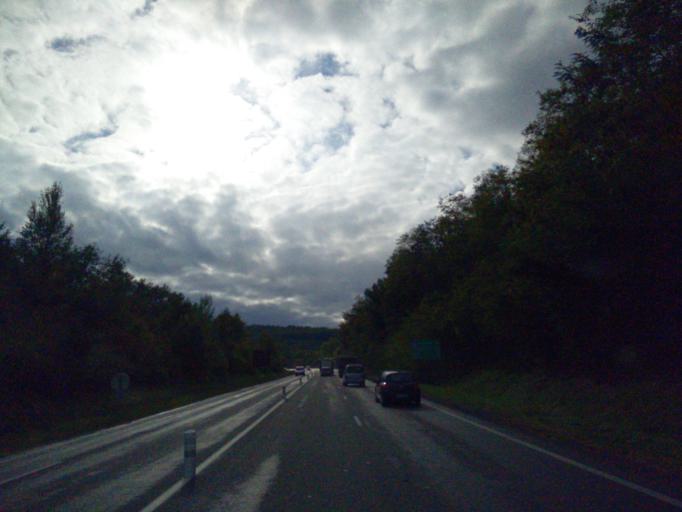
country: FR
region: Midi-Pyrenees
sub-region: Departement du Lot
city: Cahors
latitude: 44.4607
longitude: 1.4173
